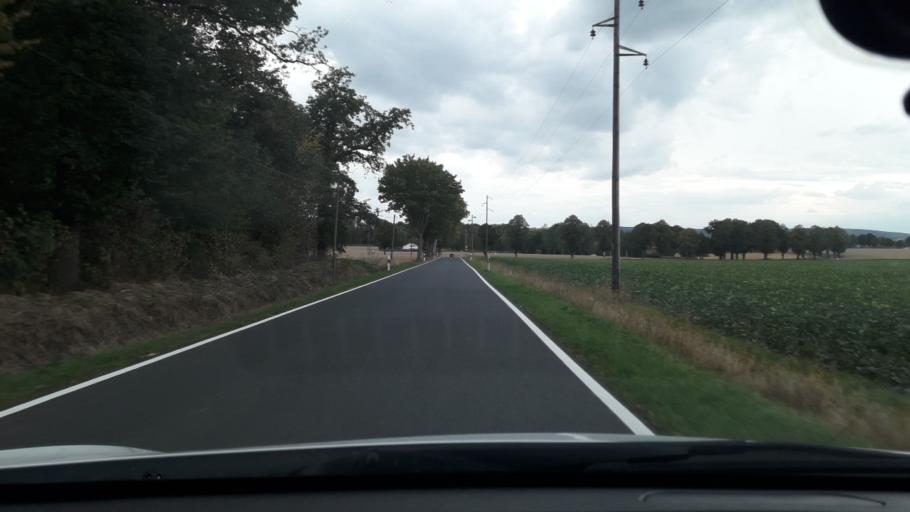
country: DE
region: Lower Saxony
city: Gielde
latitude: 52.0522
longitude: 10.4798
